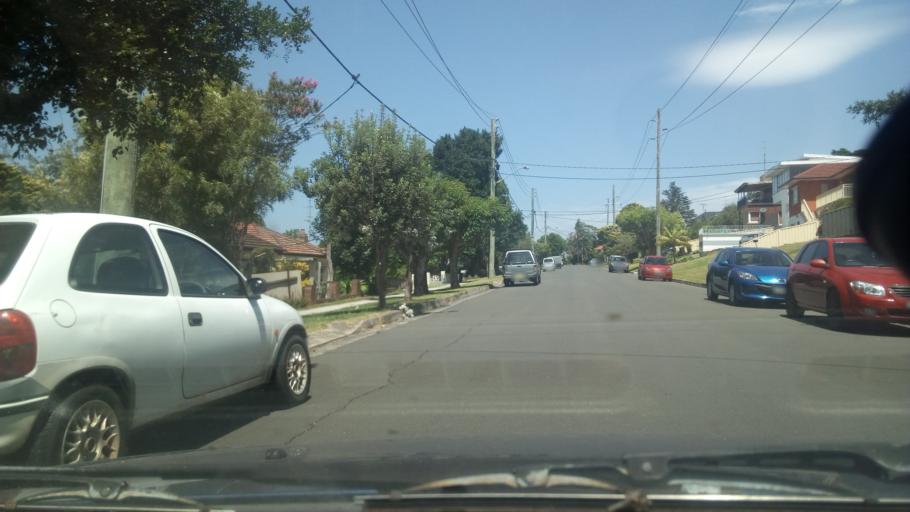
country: AU
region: New South Wales
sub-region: Wollongong
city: West Wollongong
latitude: -34.4276
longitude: 150.8661
